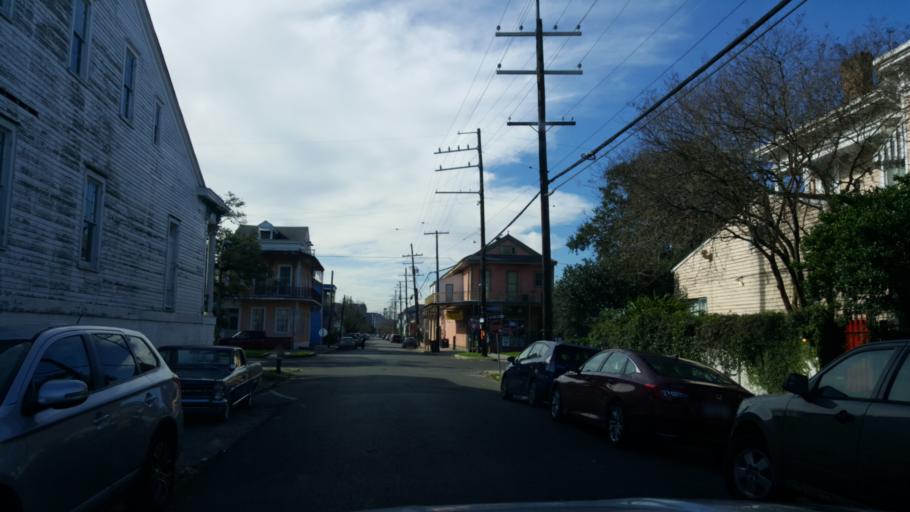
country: US
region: Louisiana
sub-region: Orleans Parish
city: New Orleans
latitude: 29.9693
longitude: -90.0661
